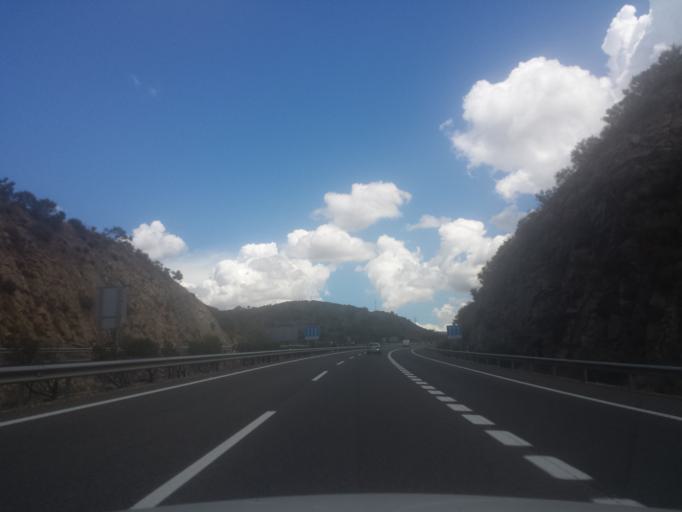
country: ES
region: Extremadura
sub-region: Provincia de Caceres
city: Aldeanueva del Camino
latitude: 40.2727
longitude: -5.9115
